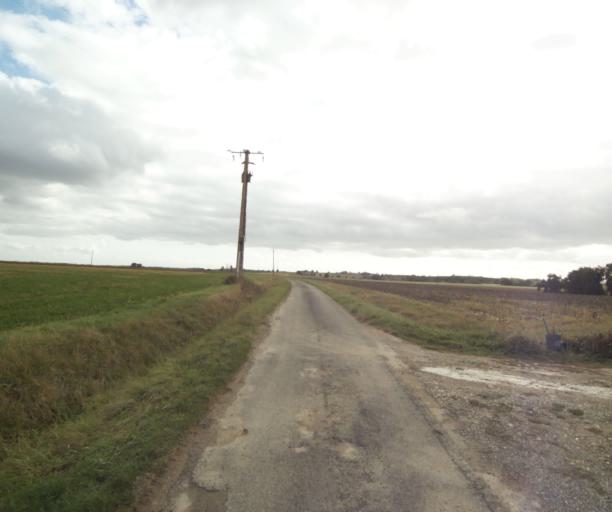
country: FR
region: Midi-Pyrenees
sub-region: Departement du Tarn-et-Garonne
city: Beaumont-de-Lomagne
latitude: 43.8897
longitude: 1.0872
